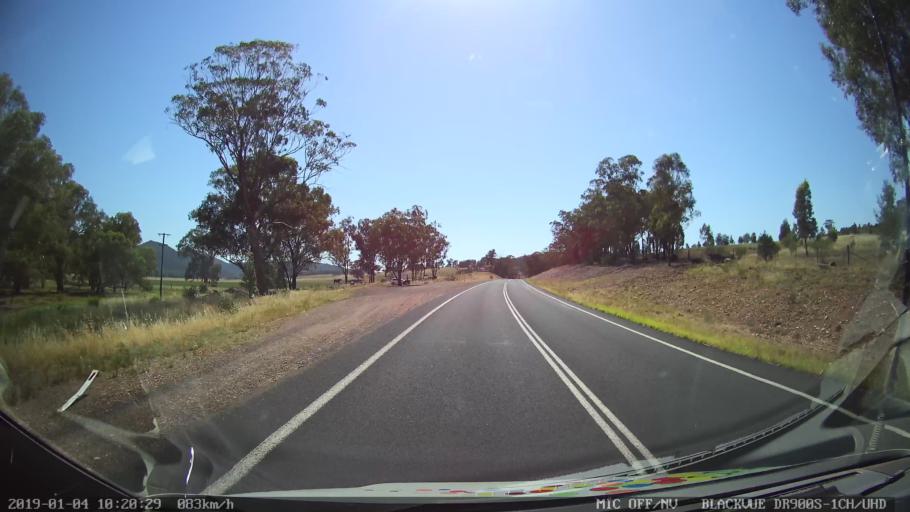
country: AU
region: New South Wales
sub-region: Cabonne
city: Canowindra
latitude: -33.3720
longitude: 148.4965
